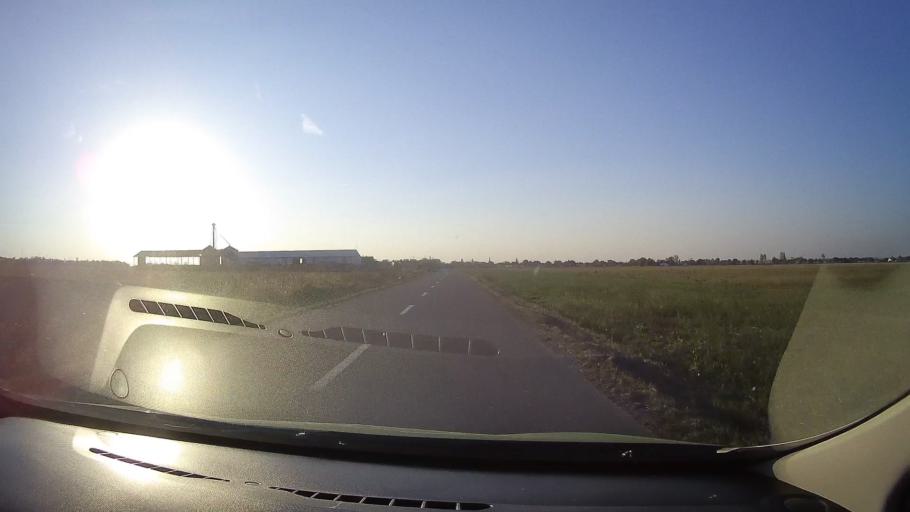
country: RO
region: Bihor
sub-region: Comuna Biharea
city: Biharea
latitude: 47.1629
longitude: 21.9579
